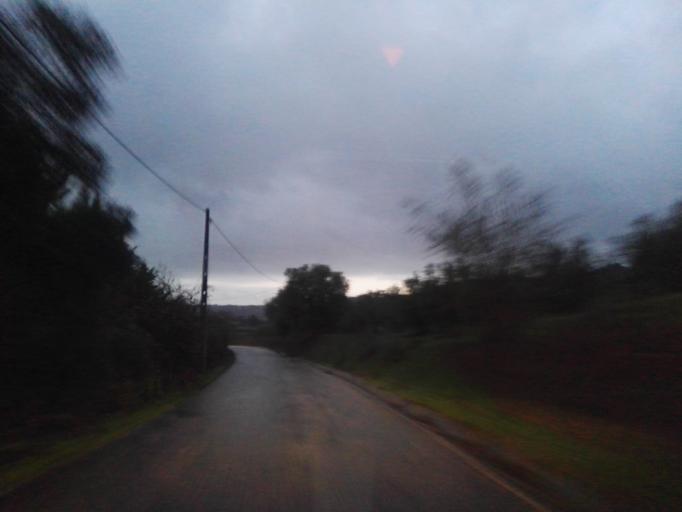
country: PT
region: Santarem
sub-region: Santarem
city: Santarem
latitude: 39.2788
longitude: -8.7923
